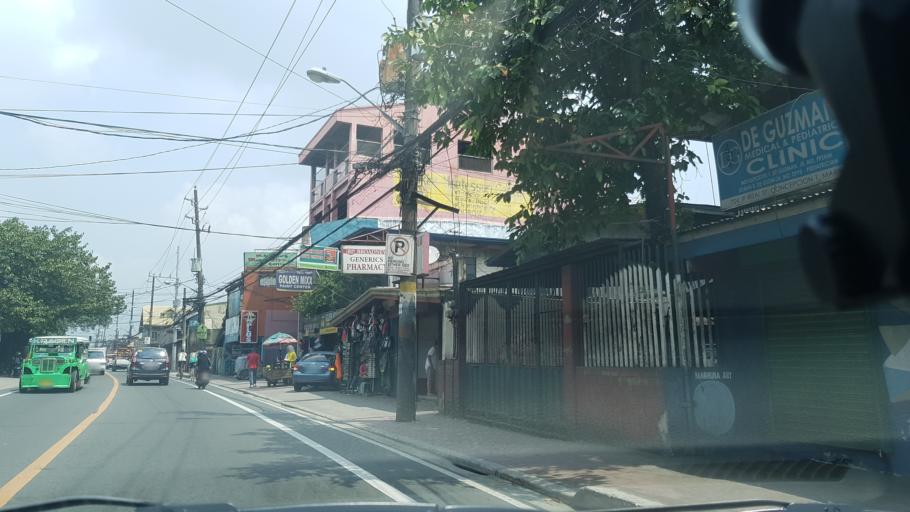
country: PH
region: Metro Manila
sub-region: Marikina
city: Calumpang
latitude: 14.6513
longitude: 121.1030
